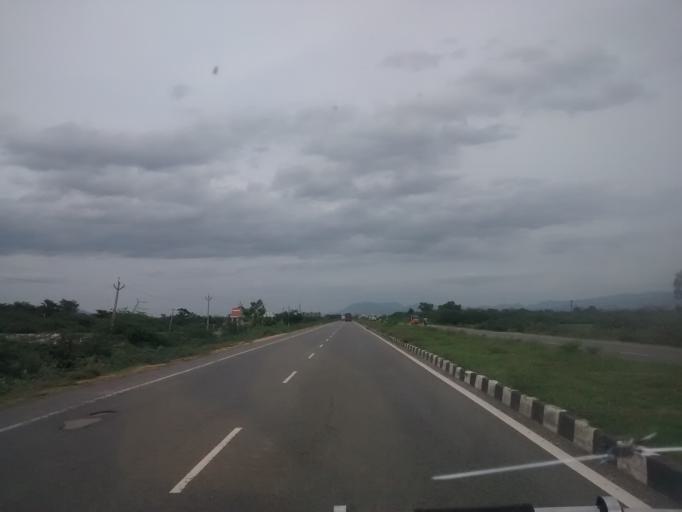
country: IN
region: Andhra Pradesh
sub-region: Chittoor
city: Tirupati
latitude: 13.6038
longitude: 79.3778
